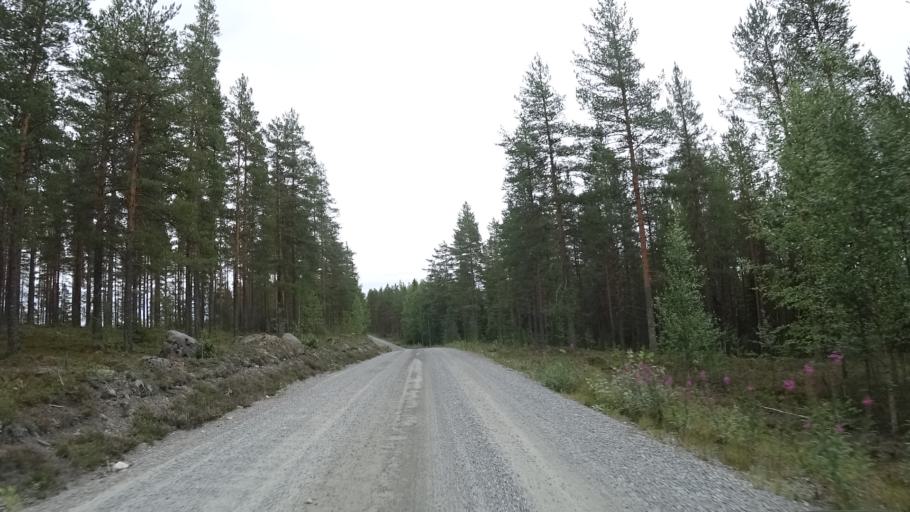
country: FI
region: North Karelia
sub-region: Pielisen Karjala
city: Lieksa
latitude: 63.3704
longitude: 30.3791
